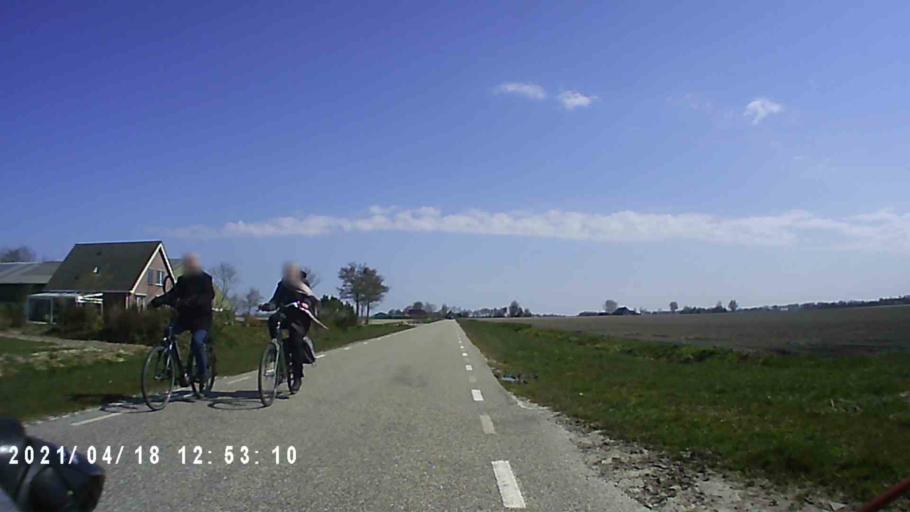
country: NL
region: Friesland
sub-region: Gemeente Dongeradeel
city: Anjum
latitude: 53.3829
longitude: 6.0649
